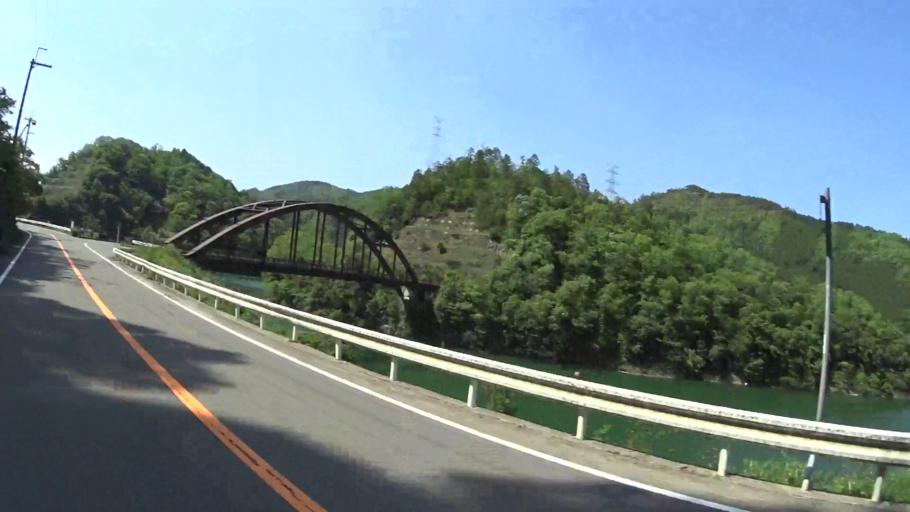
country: JP
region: Kyoto
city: Kameoka
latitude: 35.1296
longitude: 135.5582
